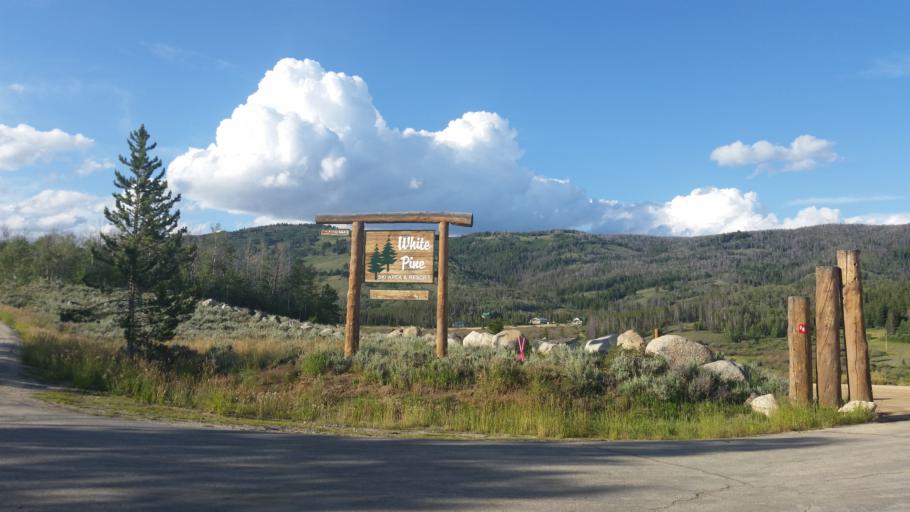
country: US
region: Wyoming
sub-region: Sublette County
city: Pinedale
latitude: 42.9699
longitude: -109.7662
